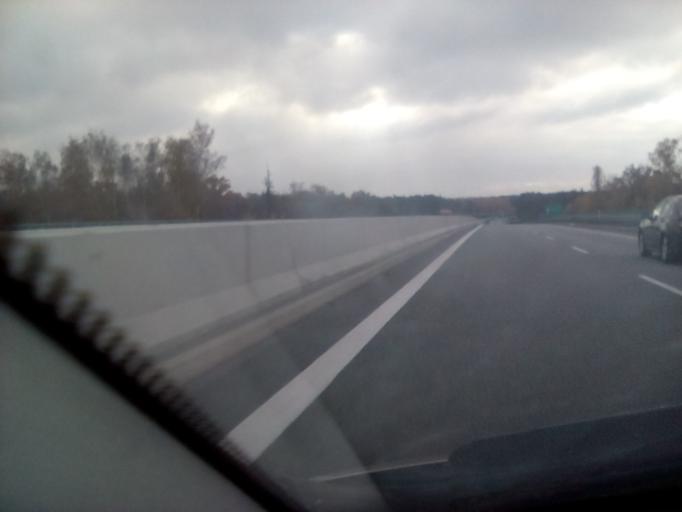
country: PL
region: Masovian Voivodeship
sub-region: Powiat bialobrzeski
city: Bialobrzegi
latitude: 51.6548
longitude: 20.9673
